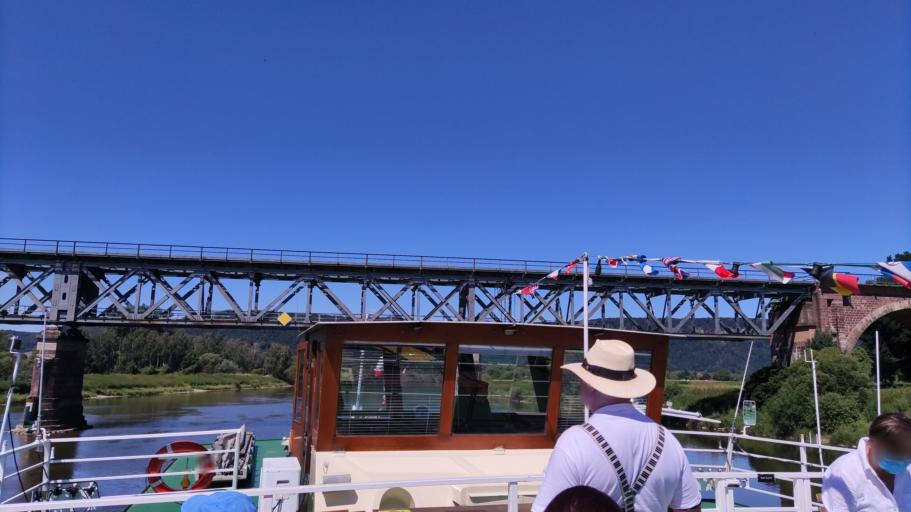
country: DE
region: Lower Saxony
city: Boffzen
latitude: 51.7362
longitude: 9.3834
